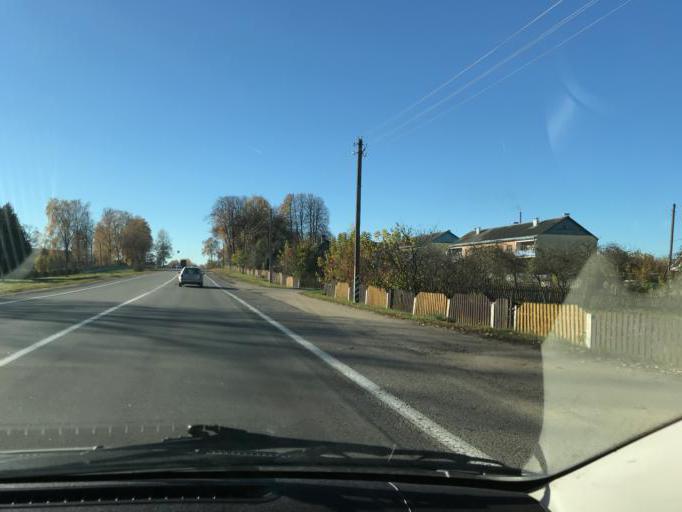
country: BY
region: Vitebsk
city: Lyepyel'
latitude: 54.9348
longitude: 28.7614
